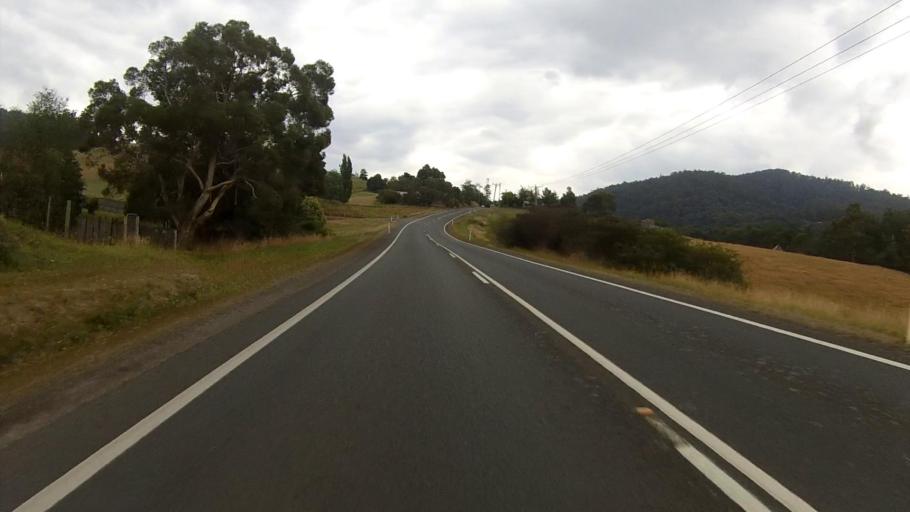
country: AU
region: Tasmania
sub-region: Huon Valley
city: Cygnet
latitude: -43.1481
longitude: 147.0677
